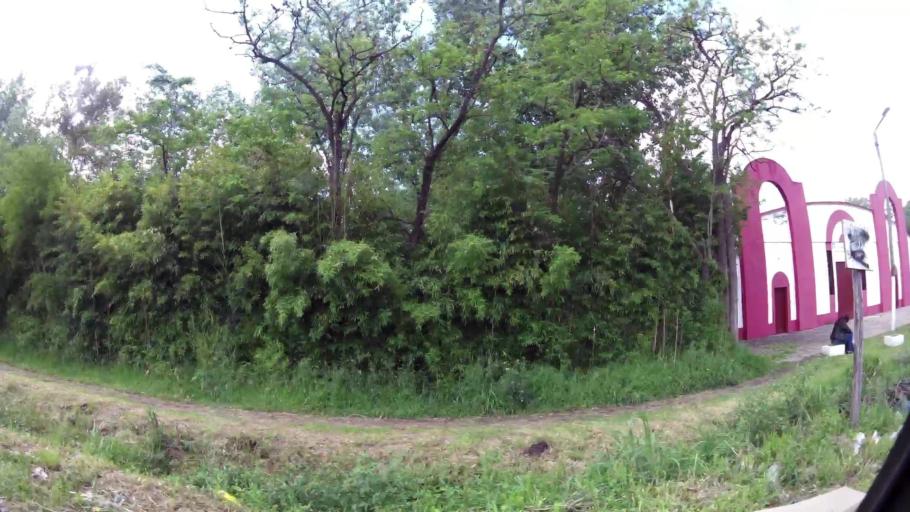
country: AR
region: Buenos Aires
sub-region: Partido de Quilmes
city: Quilmes
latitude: -34.8301
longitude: -58.2232
